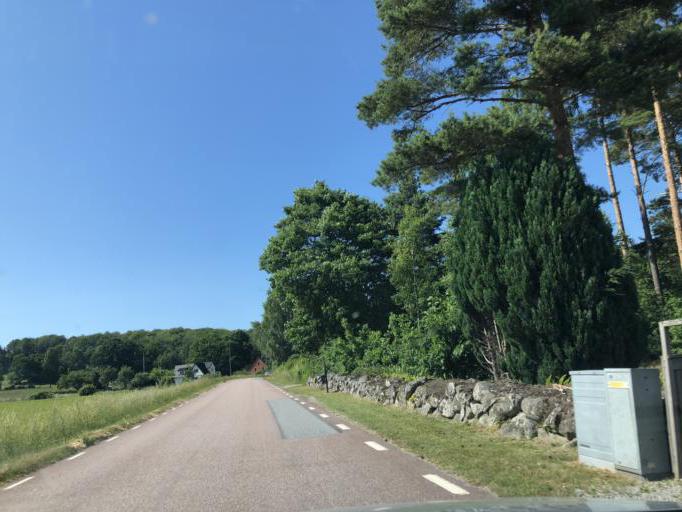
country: SE
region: Blekinge
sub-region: Solvesborgs Kommun
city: Soelvesborg
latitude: 56.1271
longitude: 14.6095
